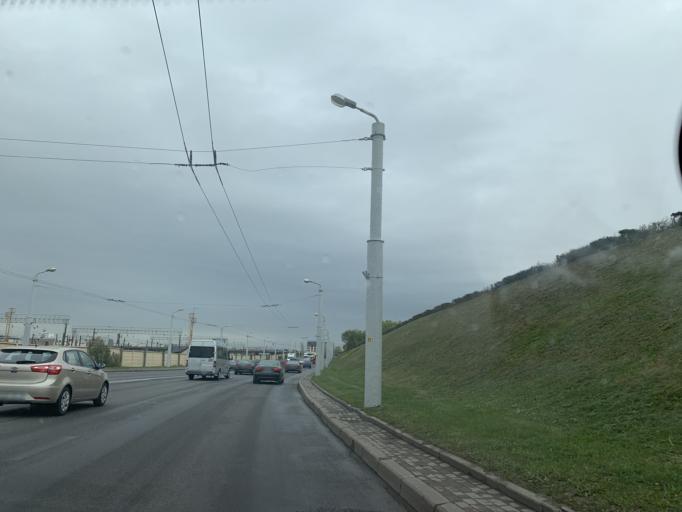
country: BY
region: Minsk
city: Syenitsa
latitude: 53.8704
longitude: 27.5229
